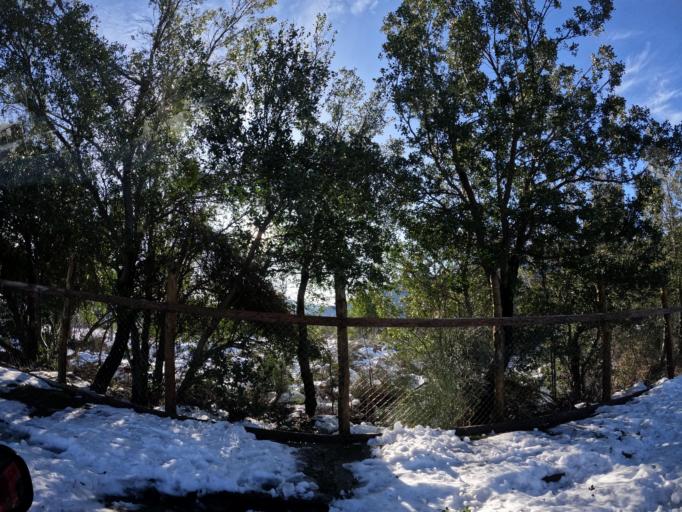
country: CL
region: Biobio
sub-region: Provincia de Nuble
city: Coihueco
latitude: -37.3708
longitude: -71.4918
